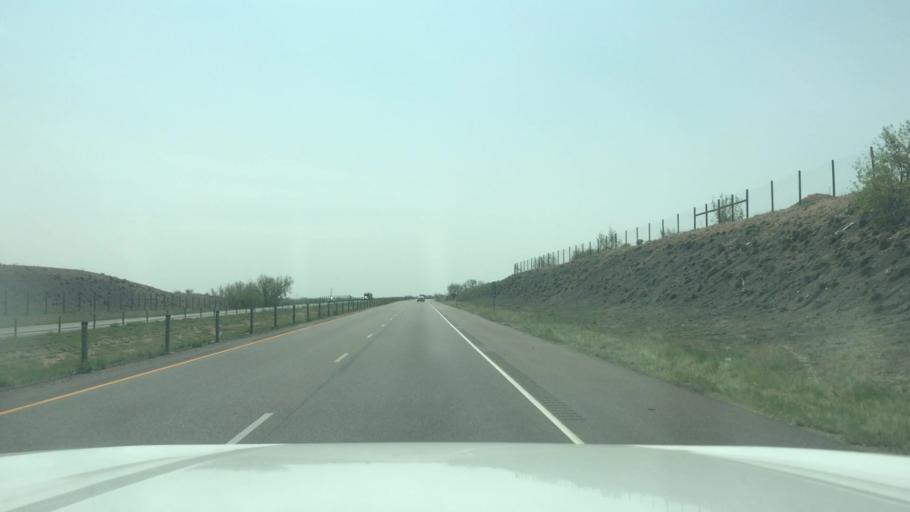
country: US
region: Colorado
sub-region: El Paso County
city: Fountain
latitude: 38.6478
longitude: -104.6956
